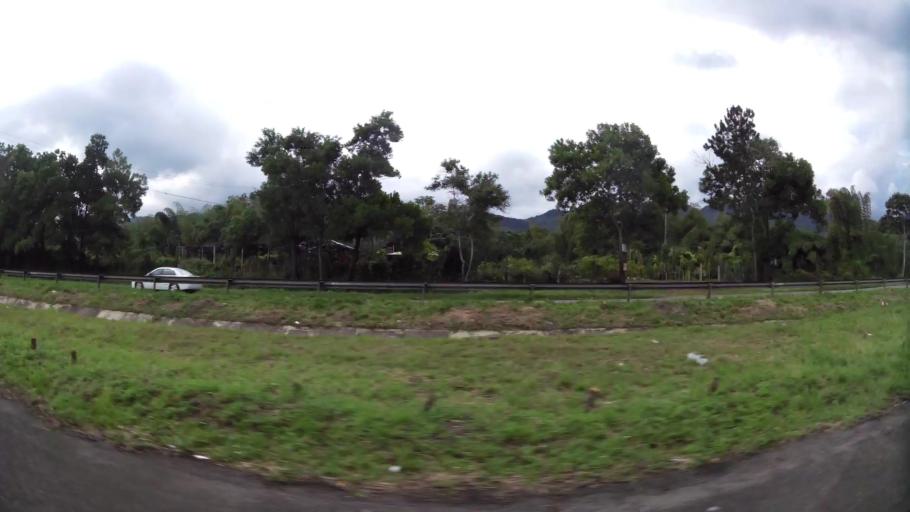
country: DO
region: Monsenor Nouel
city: Juan Adrian
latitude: 18.7748
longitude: -70.2452
